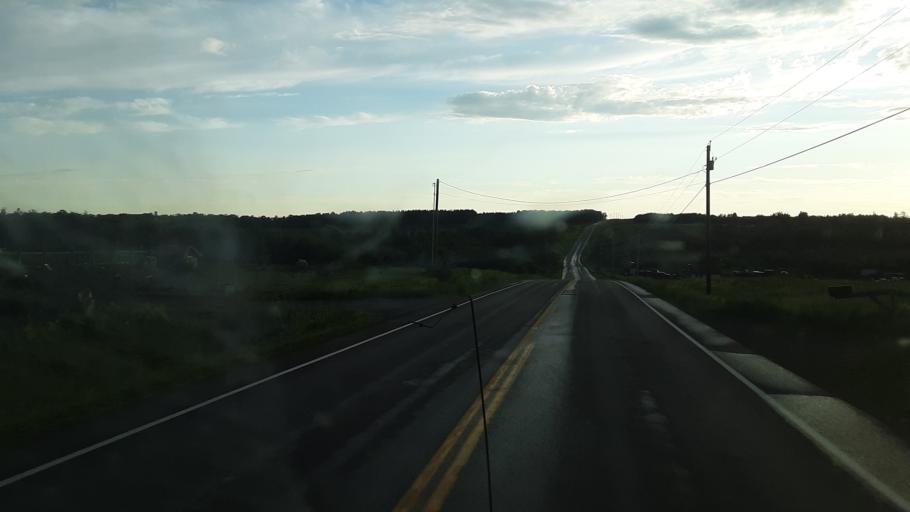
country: US
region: Maine
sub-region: Aroostook County
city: Presque Isle
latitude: 46.6751
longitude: -67.9629
